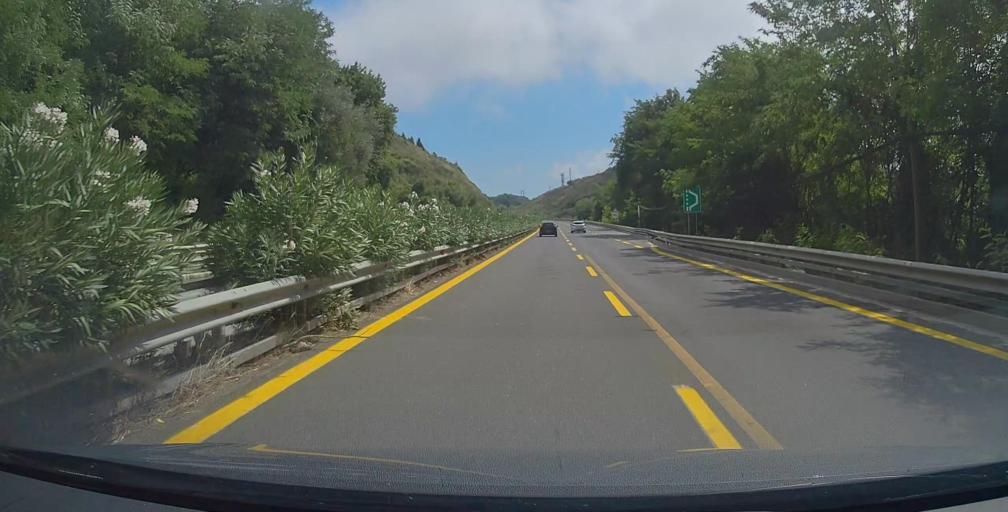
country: IT
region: Calabria
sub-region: Provincia di Vibo-Valentia
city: Sant'Onofrio
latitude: 38.7154
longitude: 16.1542
